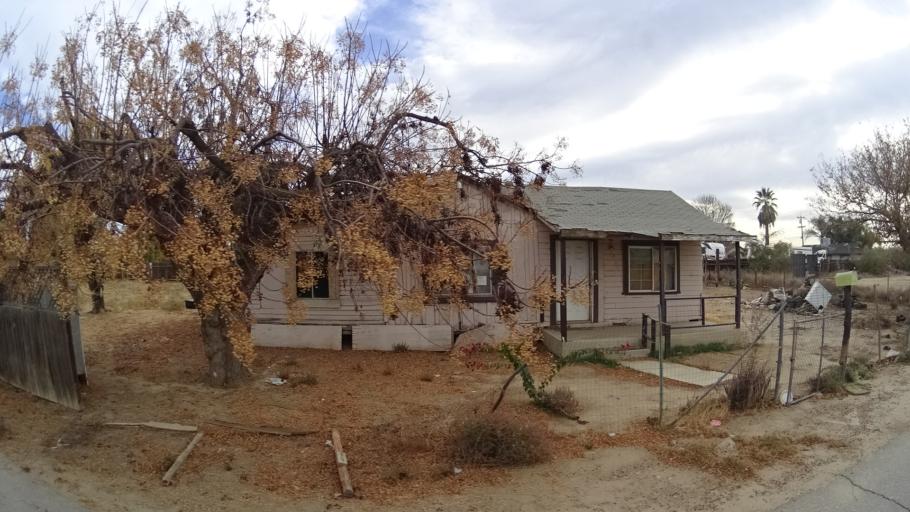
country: US
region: California
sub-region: Kern County
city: Rosedale
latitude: 35.4423
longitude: -119.2039
